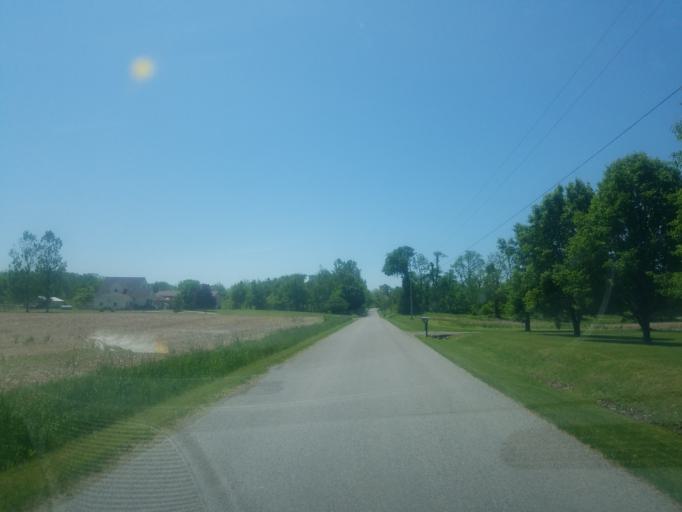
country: US
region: Ohio
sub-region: Huron County
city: Wakeman
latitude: 41.1895
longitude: -82.3701
